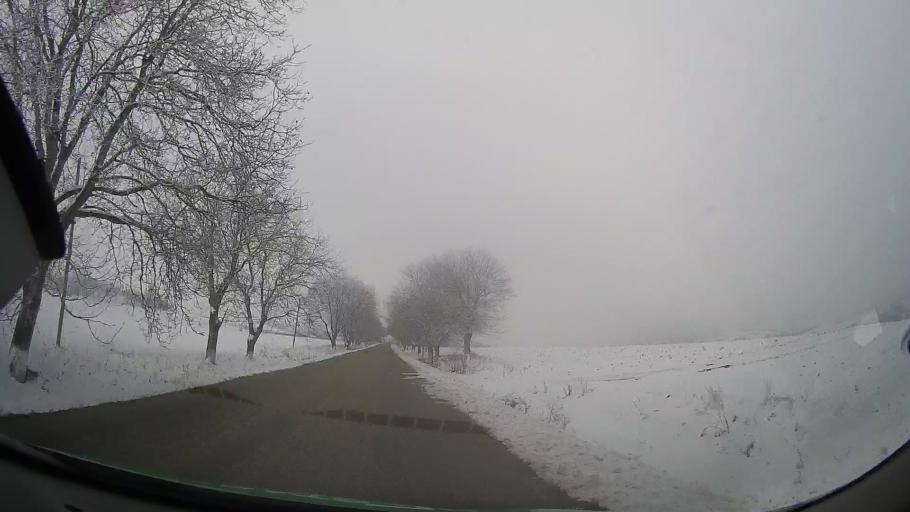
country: RO
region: Bacau
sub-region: Comuna Oncesti
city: Oncesti
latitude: 46.4476
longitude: 27.2637
